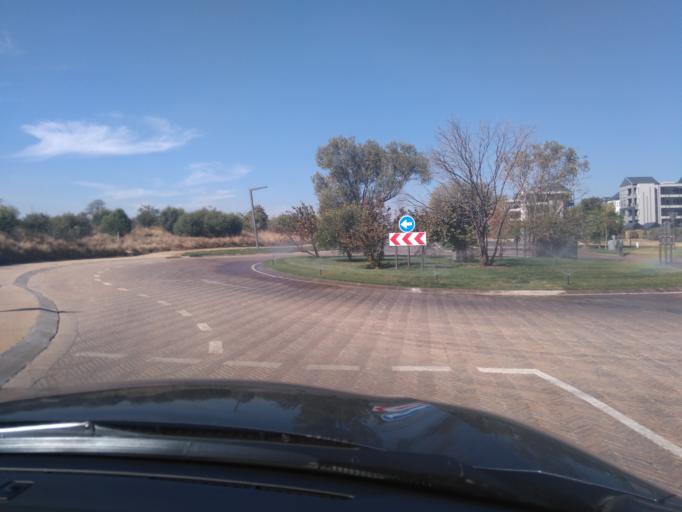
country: ZA
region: Gauteng
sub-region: City of Johannesburg Metropolitan Municipality
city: Diepsloot
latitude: -25.9681
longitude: 27.9985
